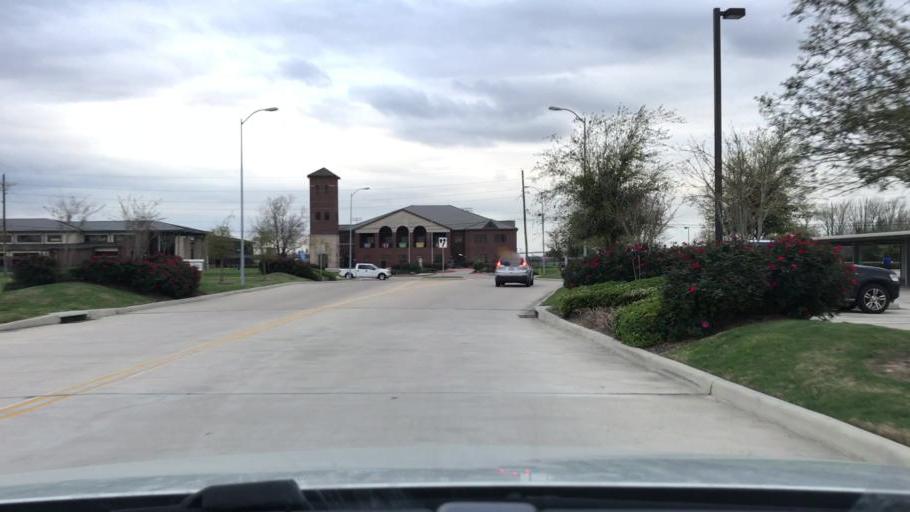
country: US
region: Texas
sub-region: Harris County
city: Katy
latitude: 29.8029
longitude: -95.7725
